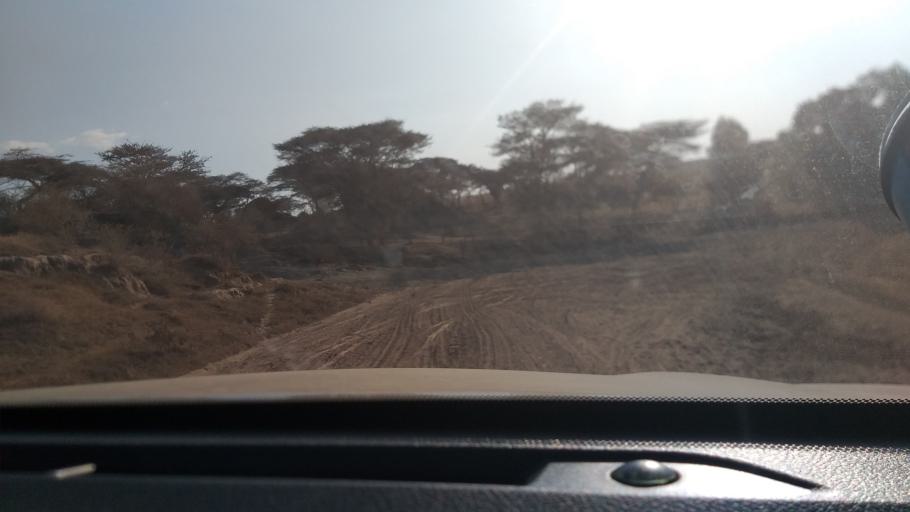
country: ET
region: Oromiya
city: Shashemene
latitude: 7.4865
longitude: 38.7250
